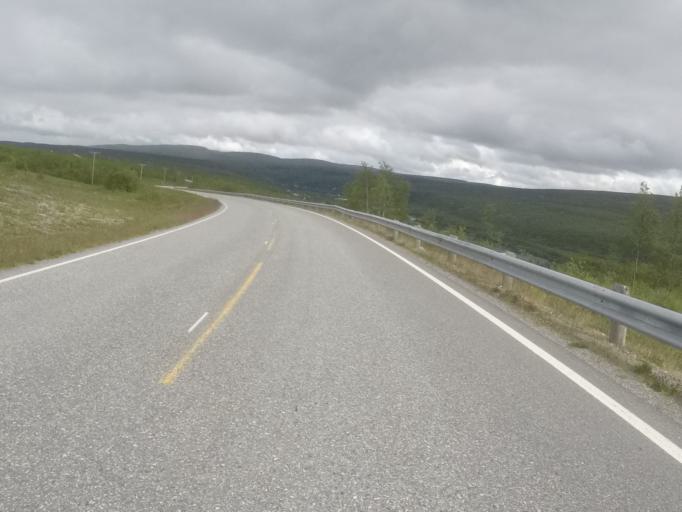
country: NO
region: Finnmark Fylke
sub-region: Alta
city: Alta
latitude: 69.4370
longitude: 23.6441
